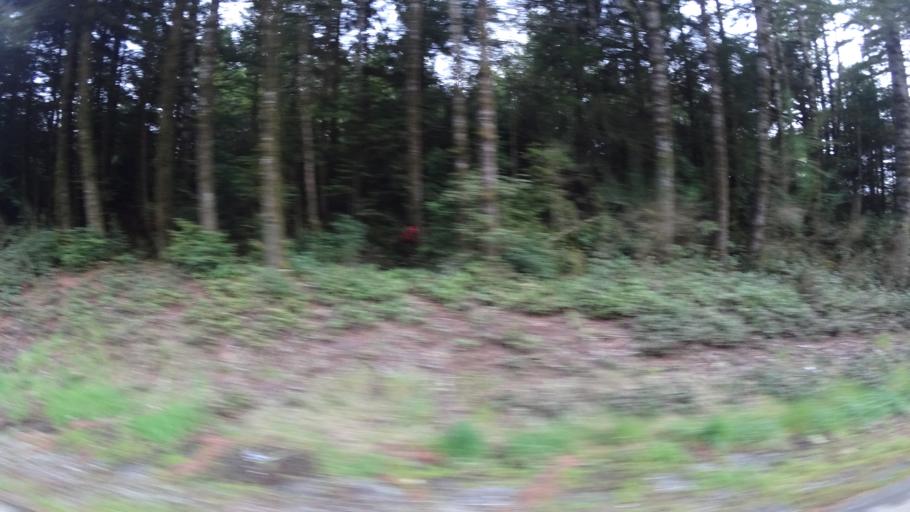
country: US
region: Oregon
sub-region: Coos County
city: Bandon
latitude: 43.1936
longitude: -124.3187
